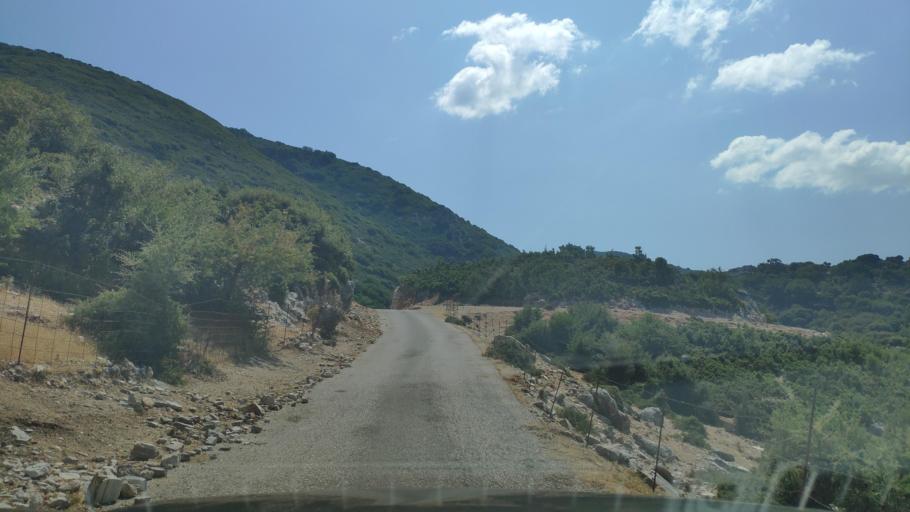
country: GR
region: West Greece
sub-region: Nomos Aitolias kai Akarnanias
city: Monastirakion
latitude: 38.8137
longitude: 20.9348
